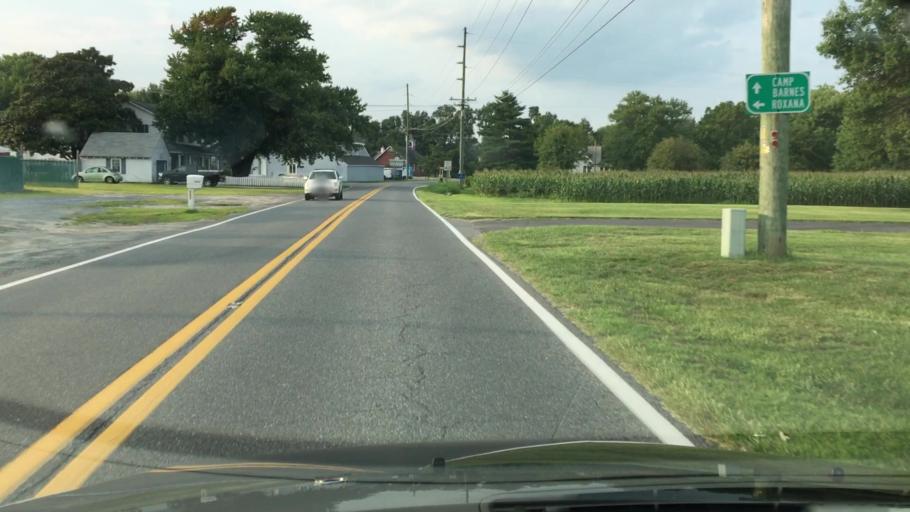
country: US
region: Delaware
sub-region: Sussex County
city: Ocean View
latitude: 38.4993
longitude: -75.1314
